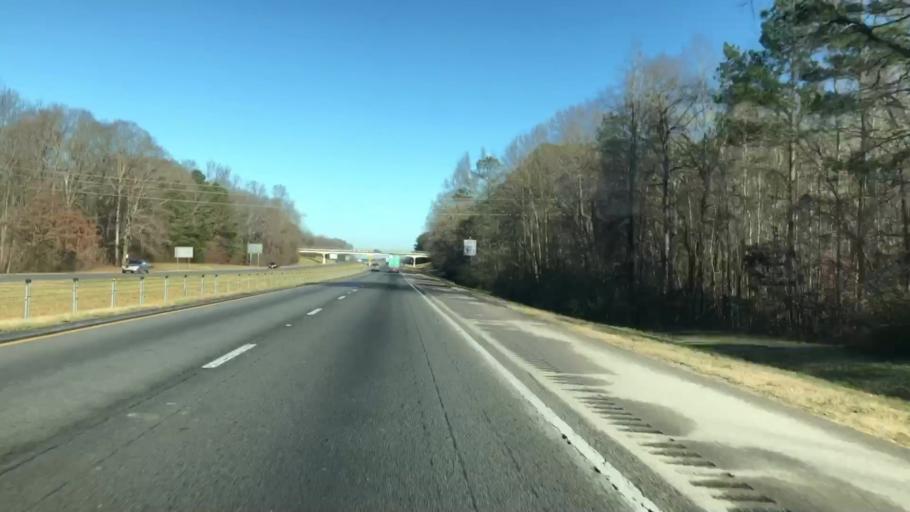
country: US
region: Alabama
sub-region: Limestone County
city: Athens
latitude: 34.7929
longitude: -86.9395
